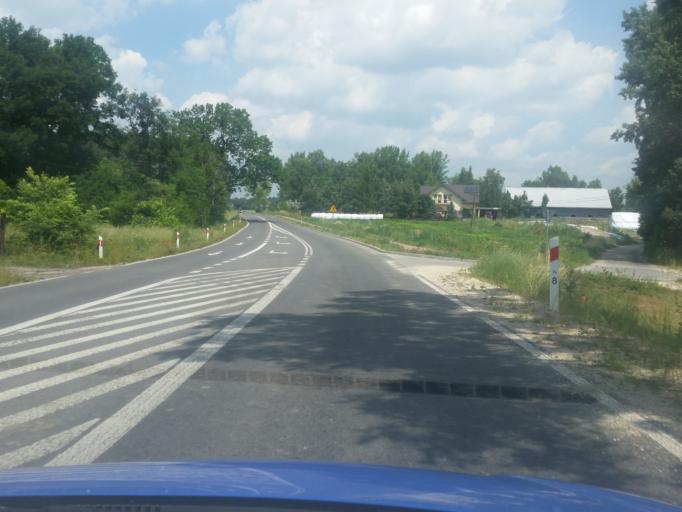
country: PL
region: Swietokrzyskie
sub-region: Powiat buski
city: Wislica
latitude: 50.3879
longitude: 20.6944
